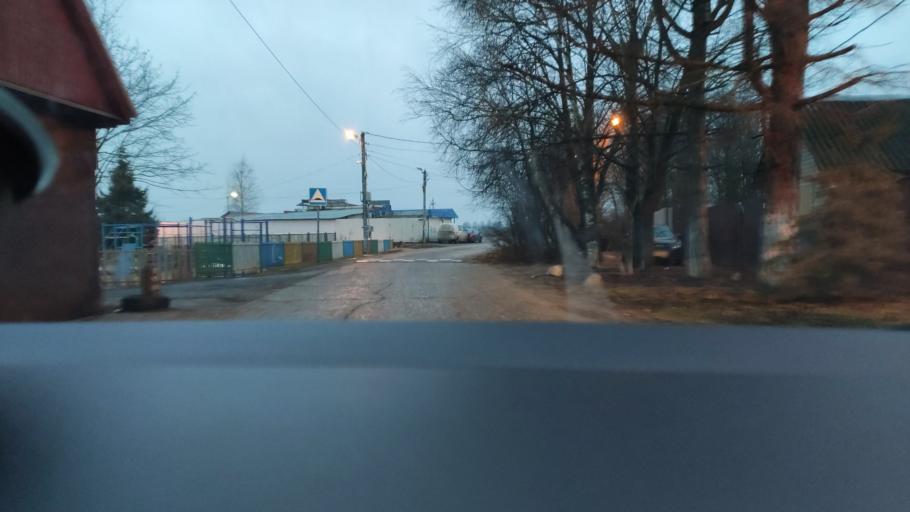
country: RU
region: Moskovskaya
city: Zvenigorod
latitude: 55.7444
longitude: 36.9361
